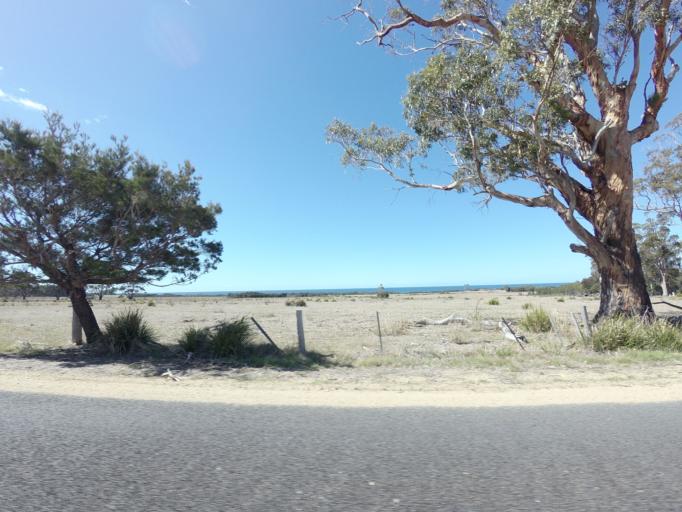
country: AU
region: Tasmania
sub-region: Break O'Day
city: St Helens
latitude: -41.7041
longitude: 148.2748
